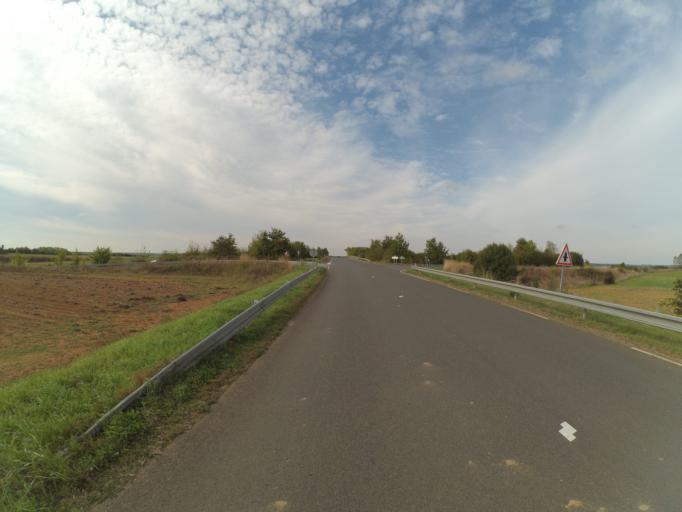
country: FR
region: Pays de la Loire
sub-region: Departement de Maine-et-Loire
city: Doue-la-Fontaine
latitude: 47.1935
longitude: -0.3159
